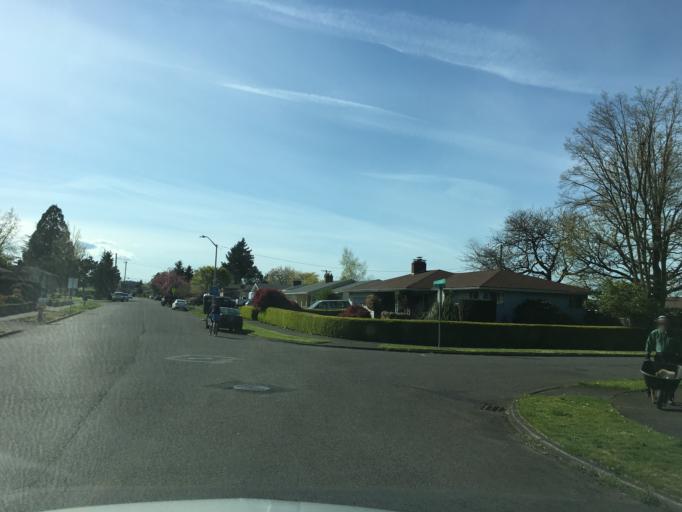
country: US
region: Oregon
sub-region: Multnomah County
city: Lents
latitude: 45.5403
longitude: -122.5148
